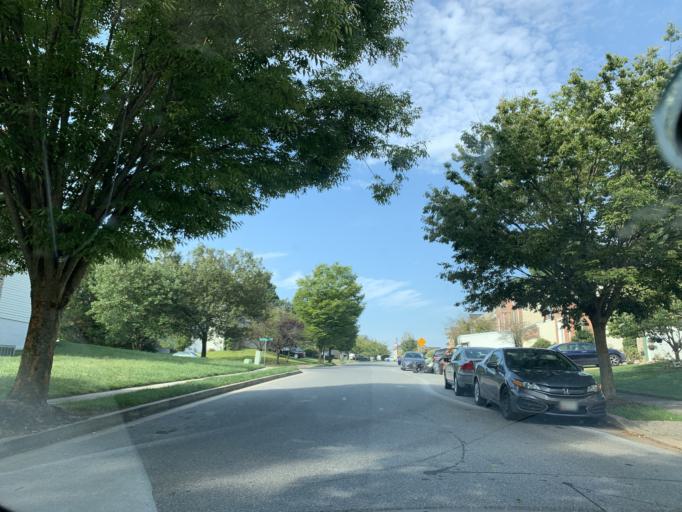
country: US
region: Maryland
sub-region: Baltimore County
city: Randallstown
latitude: 39.3894
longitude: -76.7978
